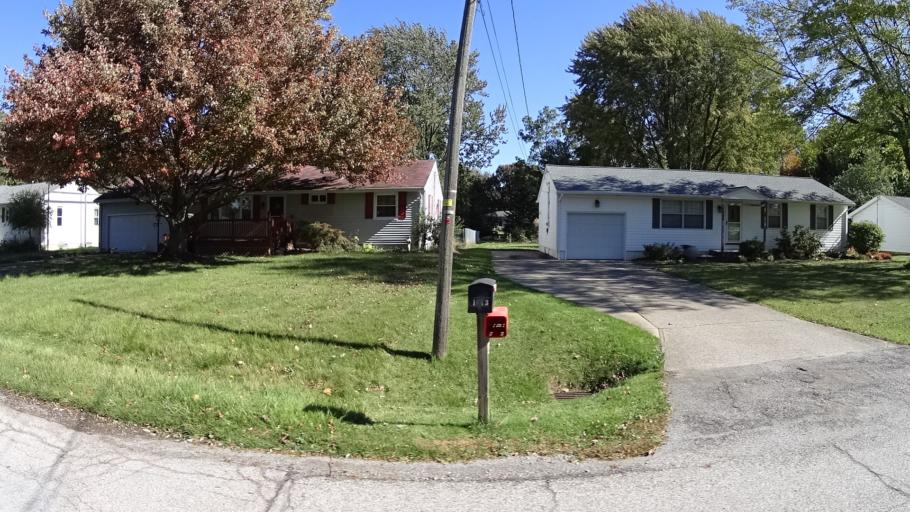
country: US
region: Ohio
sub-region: Lorain County
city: Amherst
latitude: 41.3830
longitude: -82.2211
